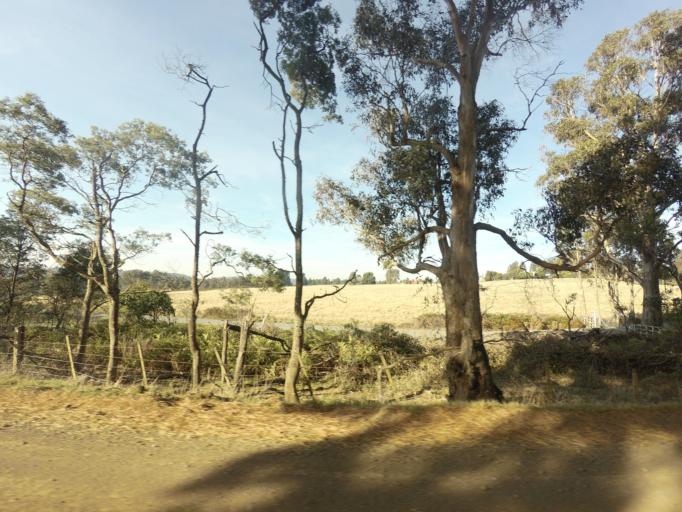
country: AU
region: Tasmania
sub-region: Brighton
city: Bridgewater
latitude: -42.4850
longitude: 147.3868
